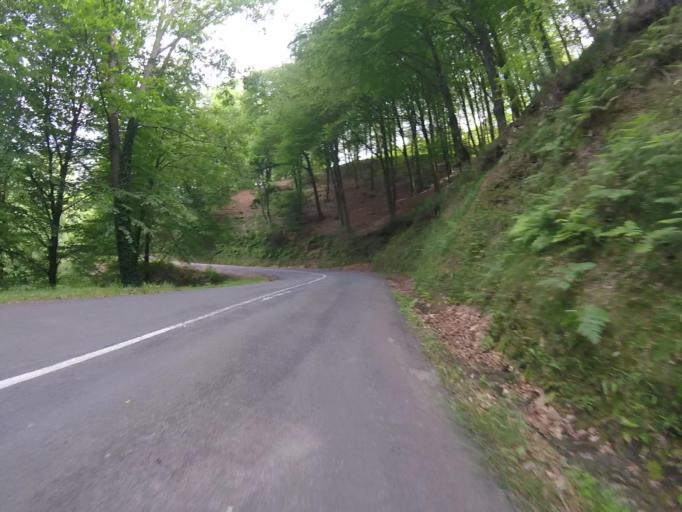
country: ES
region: Navarre
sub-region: Provincia de Navarra
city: Arano
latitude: 43.2531
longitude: -1.8499
